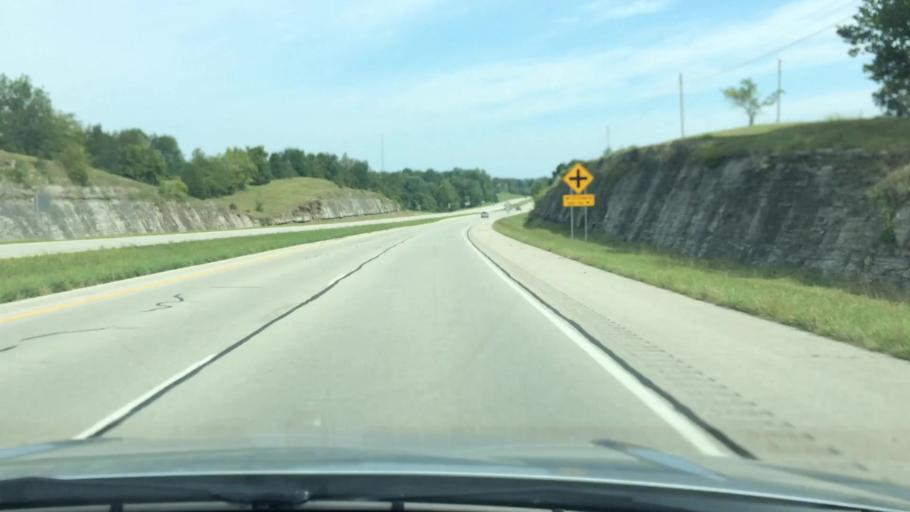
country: US
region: Kentucky
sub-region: Anderson County
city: Lawrenceburg
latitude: 38.0953
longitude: -84.9196
